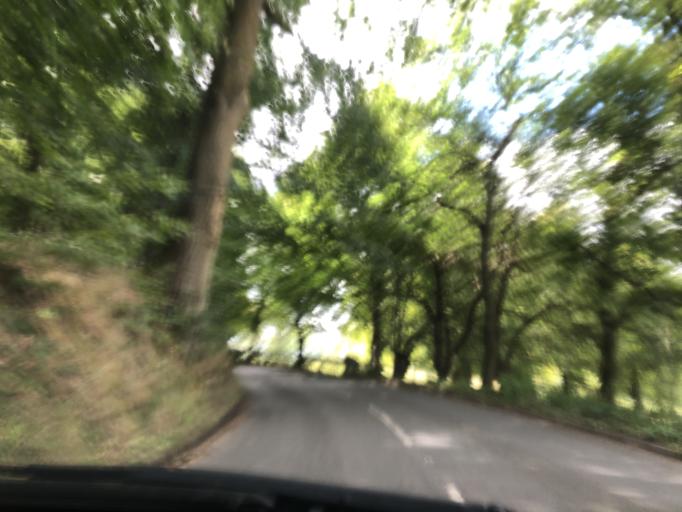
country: GB
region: England
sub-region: Kent
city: Westerham
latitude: 51.2434
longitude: 0.0738
